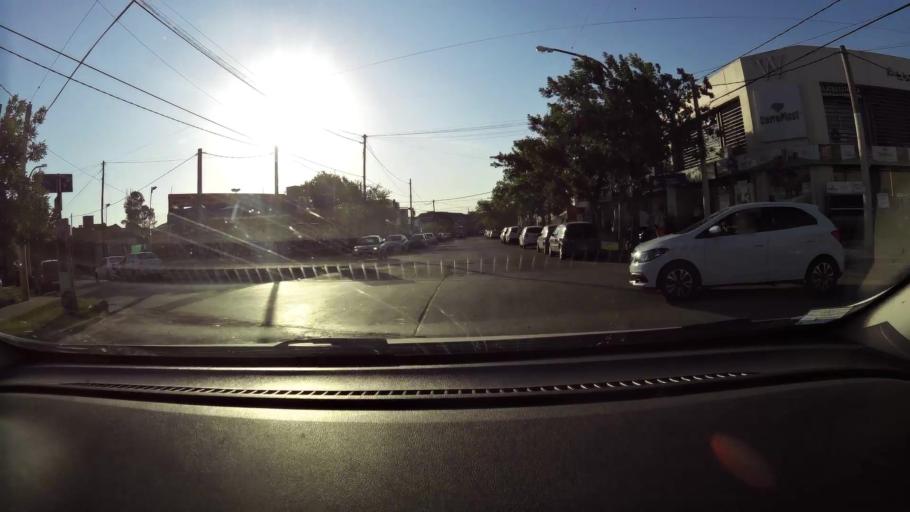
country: AR
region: Cordoba
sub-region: Departamento de Capital
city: Cordoba
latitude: -31.3822
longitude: -64.2386
